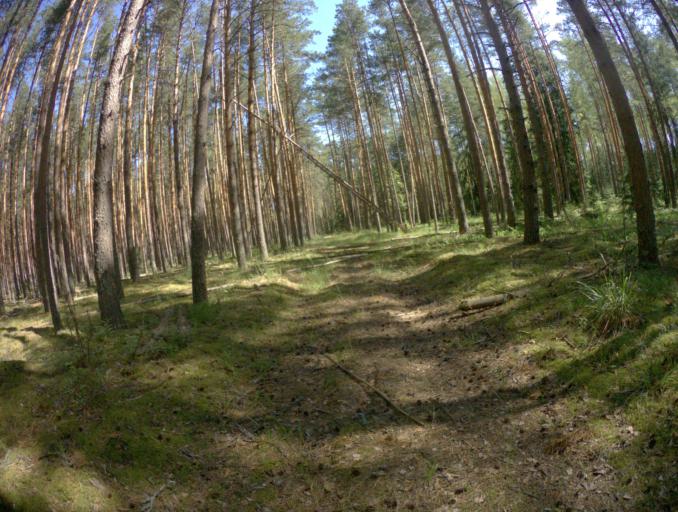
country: RU
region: Ivanovo
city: Talitsy
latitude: 56.3393
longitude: 42.3279
